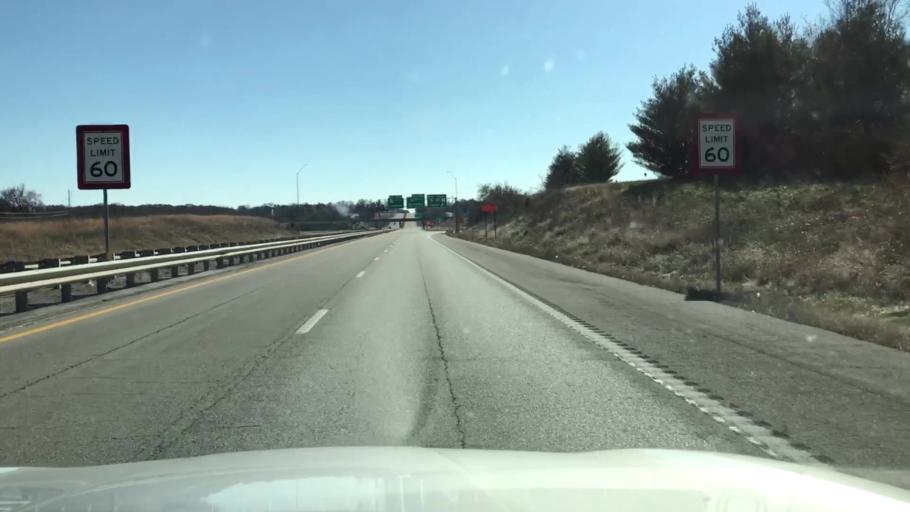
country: US
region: Missouri
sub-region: Jasper County
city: Carthage
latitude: 37.0869
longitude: -94.3124
